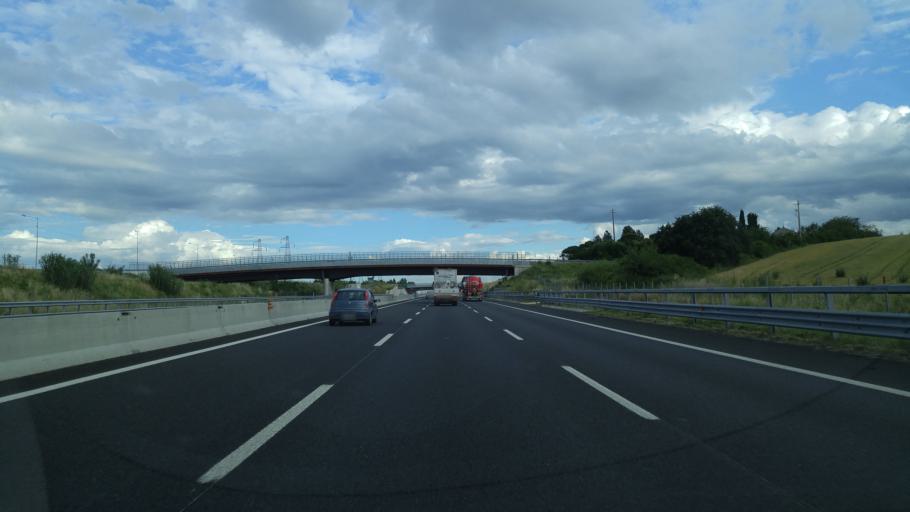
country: IT
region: Emilia-Romagna
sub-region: Provincia di Rimini
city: Rivazzurra
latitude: 44.0112
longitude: 12.5935
